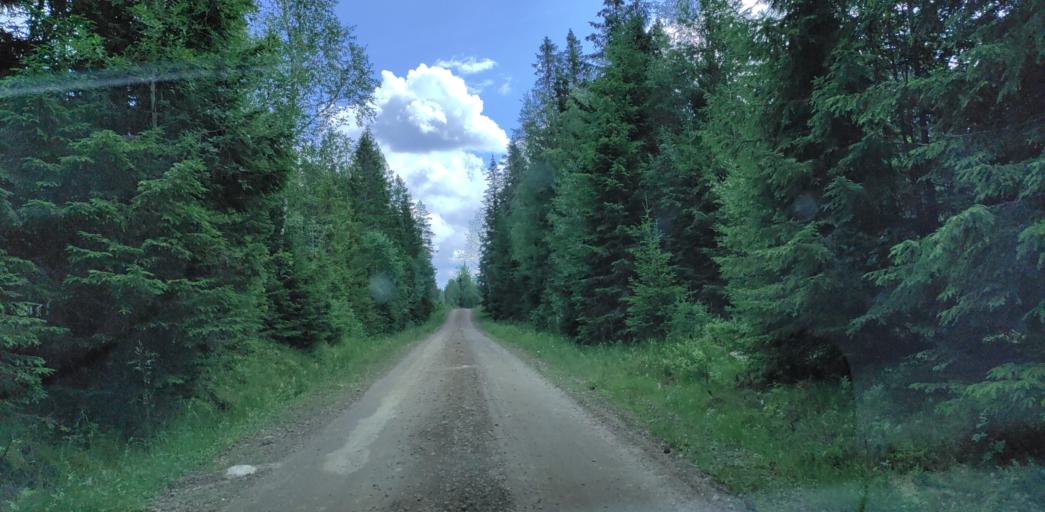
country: SE
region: Vaermland
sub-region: Hagfors Kommun
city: Ekshaerad
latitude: 60.0903
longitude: 13.3431
